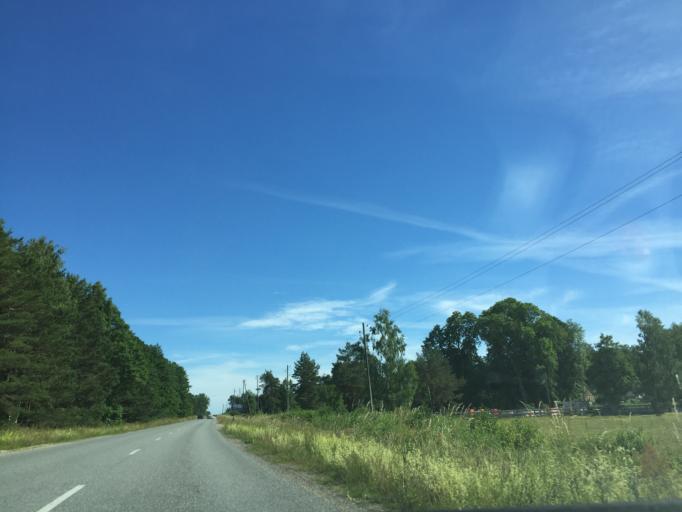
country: LV
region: Rojas
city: Roja
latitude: 57.4784
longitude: 22.8614
